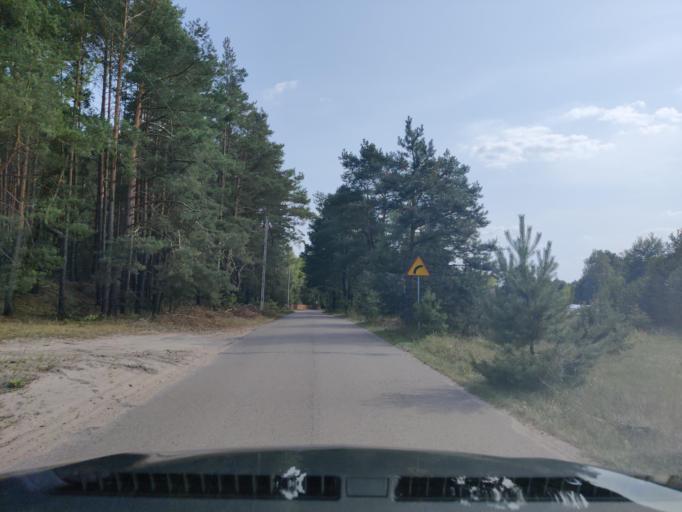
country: PL
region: Masovian Voivodeship
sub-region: Powiat makowski
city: Rozan
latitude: 52.8523
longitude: 21.4565
